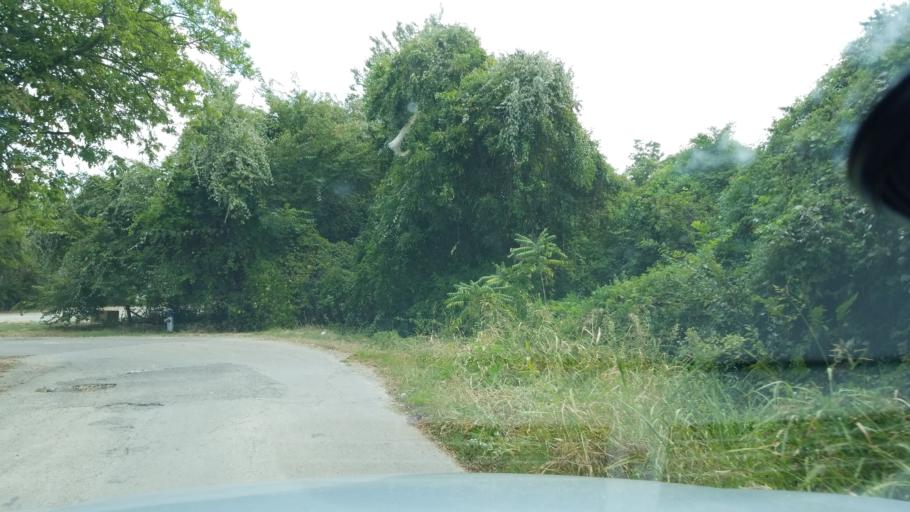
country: US
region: Texas
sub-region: Dallas County
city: Dallas
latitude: 32.7753
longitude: -96.8335
